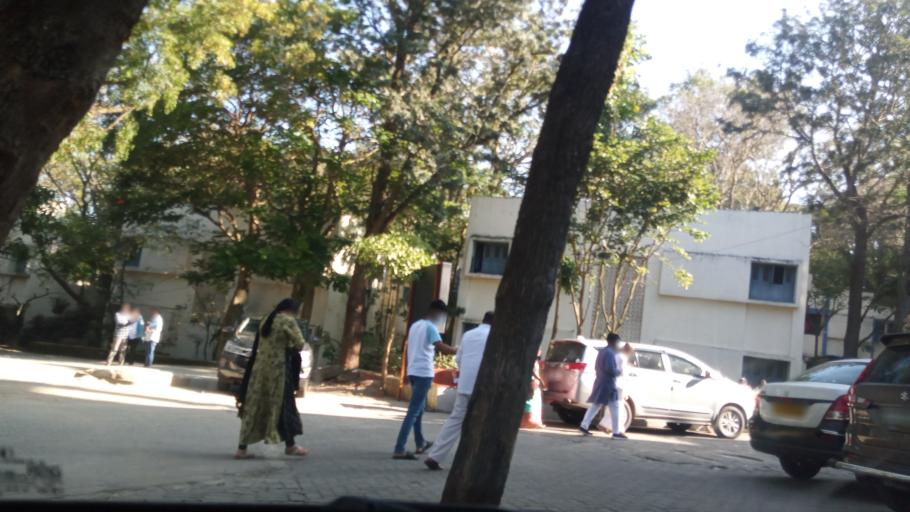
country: IN
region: Andhra Pradesh
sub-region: Chittoor
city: Tirumala
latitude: 13.6720
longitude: 79.3486
